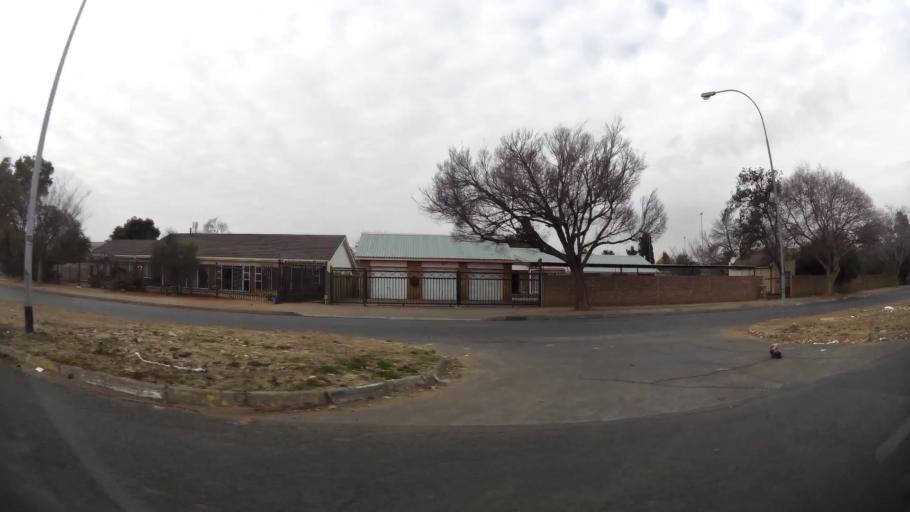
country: ZA
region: Orange Free State
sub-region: Mangaung Metropolitan Municipality
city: Bloemfontein
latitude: -29.1190
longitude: 26.1767
